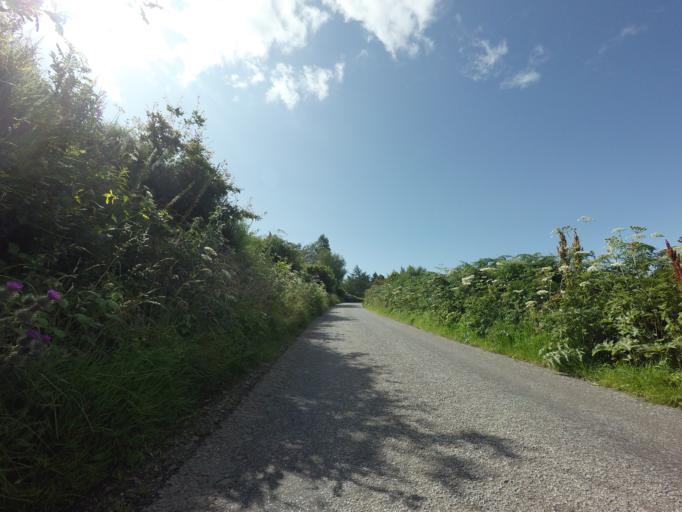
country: GB
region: Scotland
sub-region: Highland
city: Nairn
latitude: 57.5401
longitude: -3.8660
